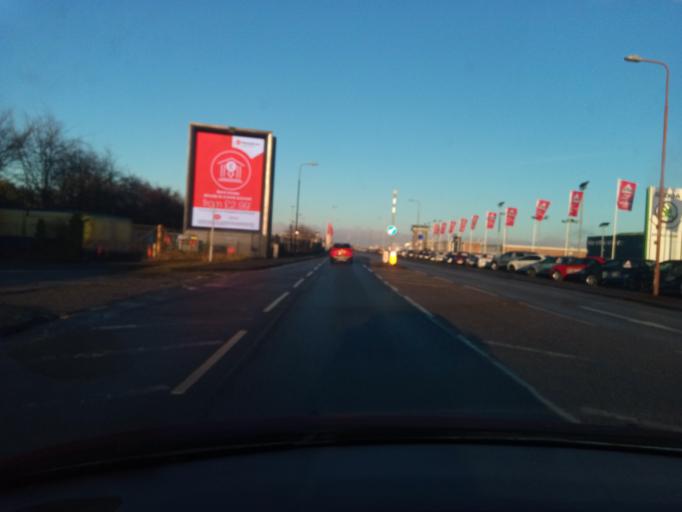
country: GB
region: Scotland
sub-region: West Lothian
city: Seafield
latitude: 55.9601
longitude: -3.1256
